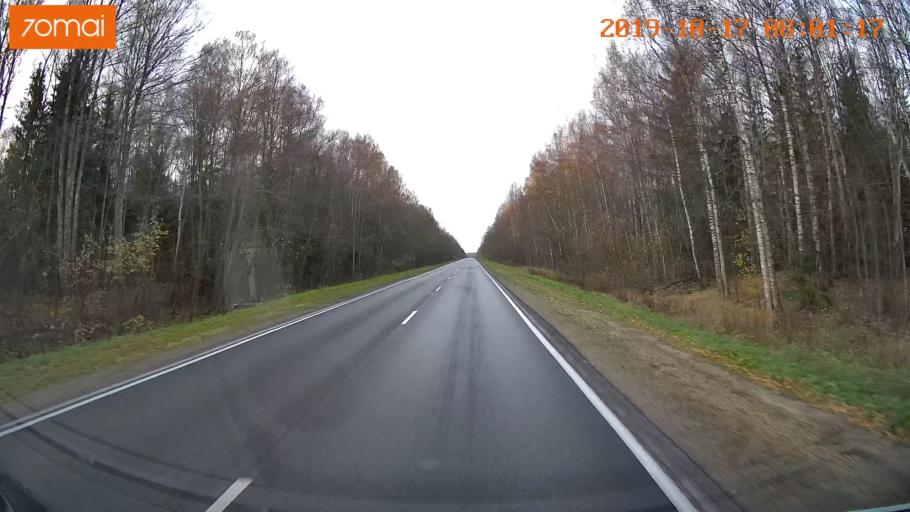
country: RU
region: Vladimir
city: Bavleny
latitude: 56.3746
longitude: 39.4999
